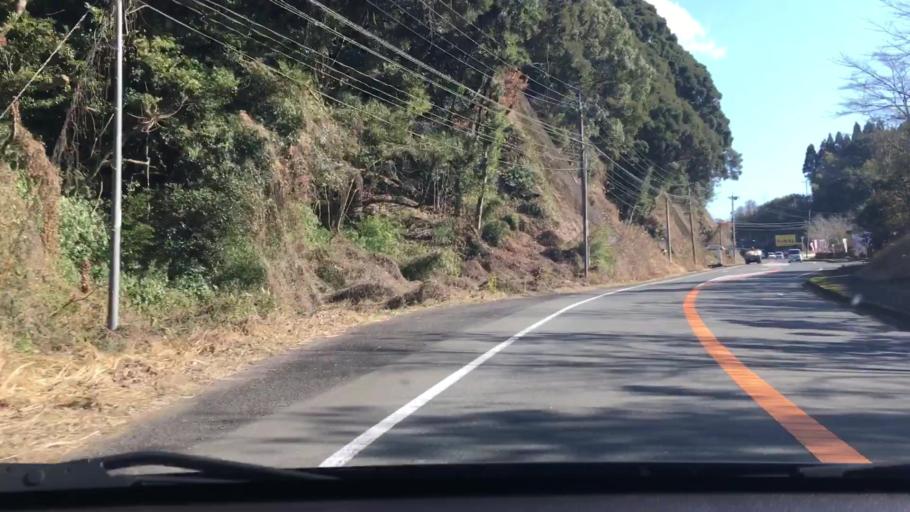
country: JP
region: Kagoshima
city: Satsumasendai
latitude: 31.7980
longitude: 130.4191
